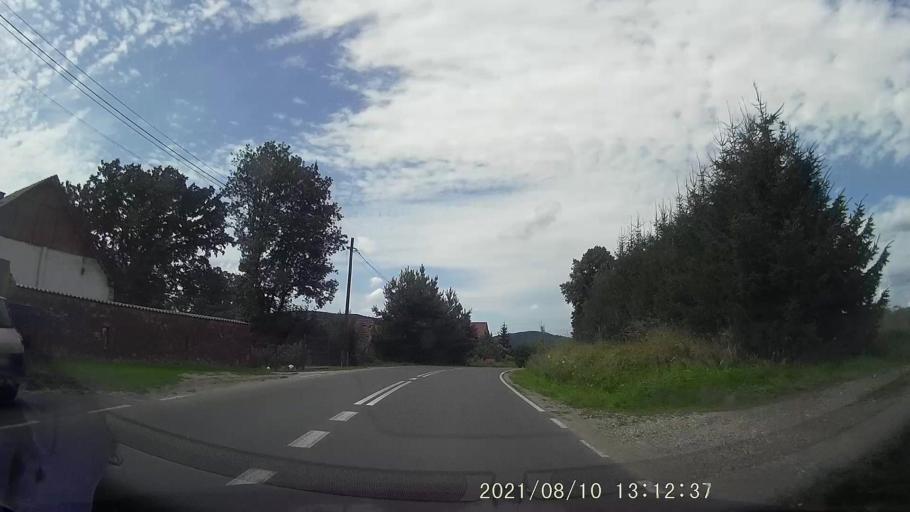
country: PL
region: Lower Silesian Voivodeship
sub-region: Powiat klodzki
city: Bozkow
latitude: 50.5166
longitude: 16.5113
